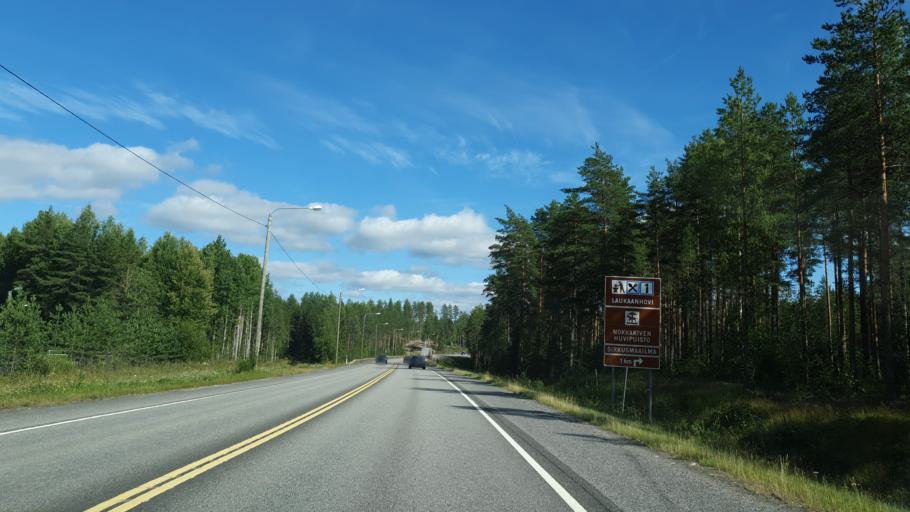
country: FI
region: Central Finland
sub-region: Jyvaeskylae
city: Toivakka
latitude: 62.2513
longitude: 26.1163
